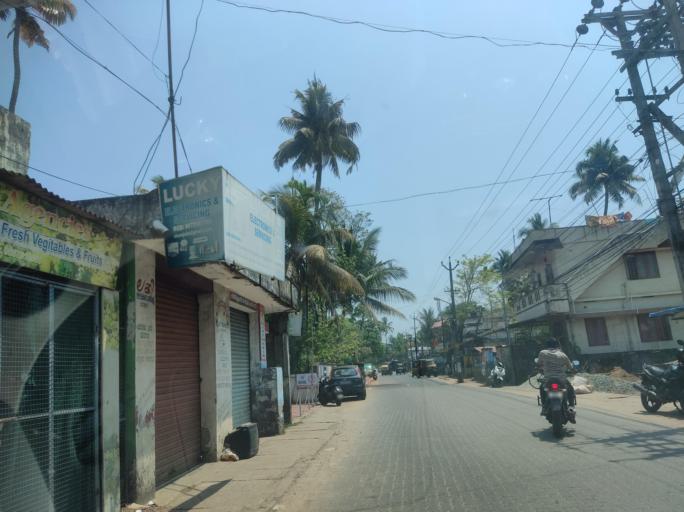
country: IN
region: Kerala
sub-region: Ernakulam
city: Cochin
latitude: 9.8938
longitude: 76.2846
